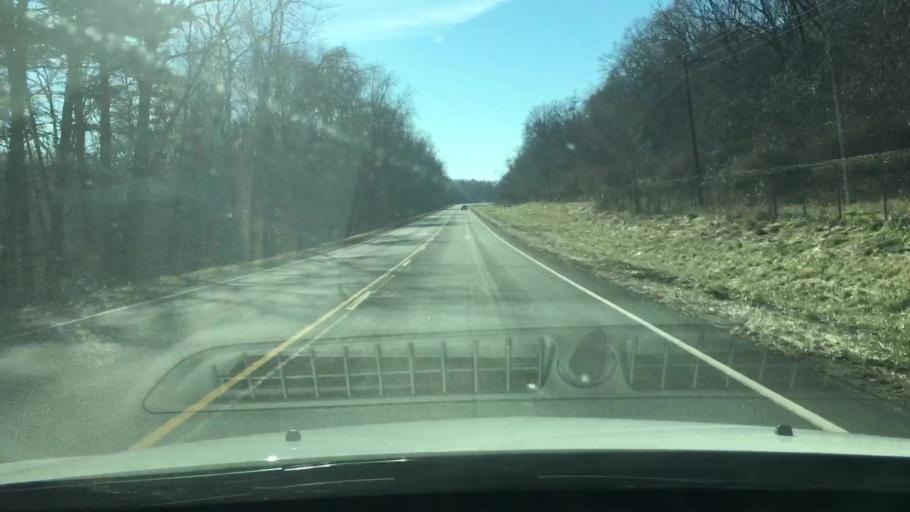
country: US
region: Illinois
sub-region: Fulton County
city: Canton
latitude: 40.4534
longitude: -89.9615
